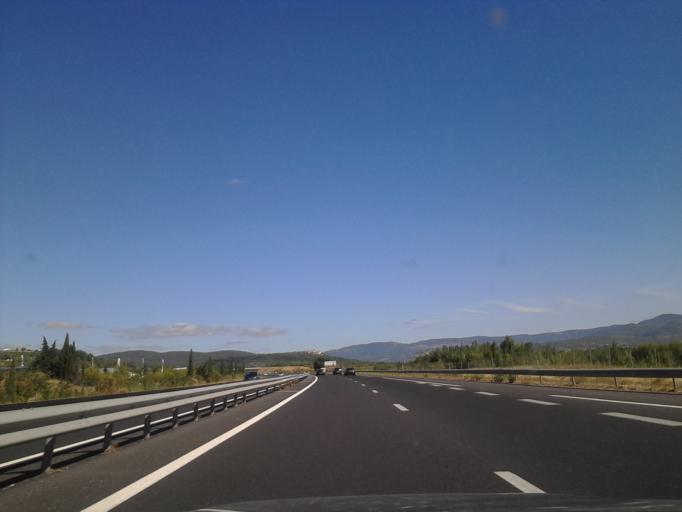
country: FR
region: Languedoc-Roussillon
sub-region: Departement de l'Herault
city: Nebian
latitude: 43.6176
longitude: 3.4589
